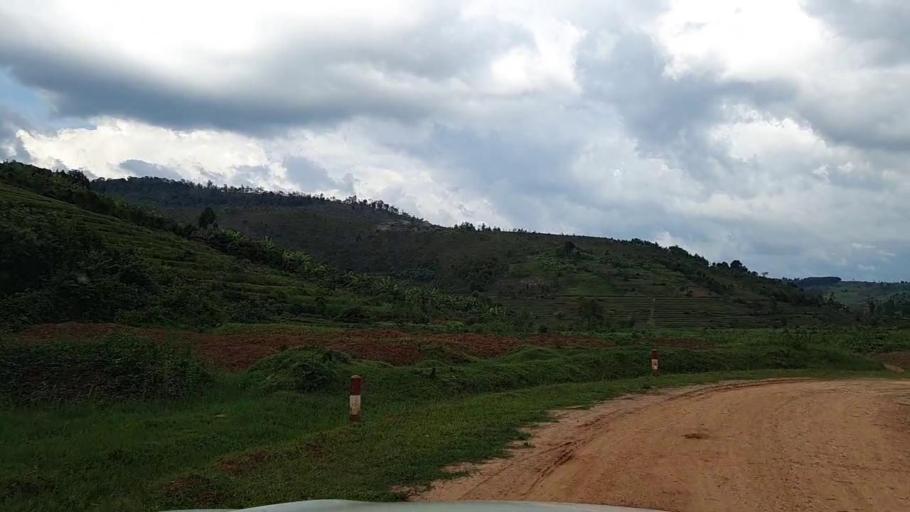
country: RW
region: Southern Province
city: Nyanza
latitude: -2.3916
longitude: 29.6837
